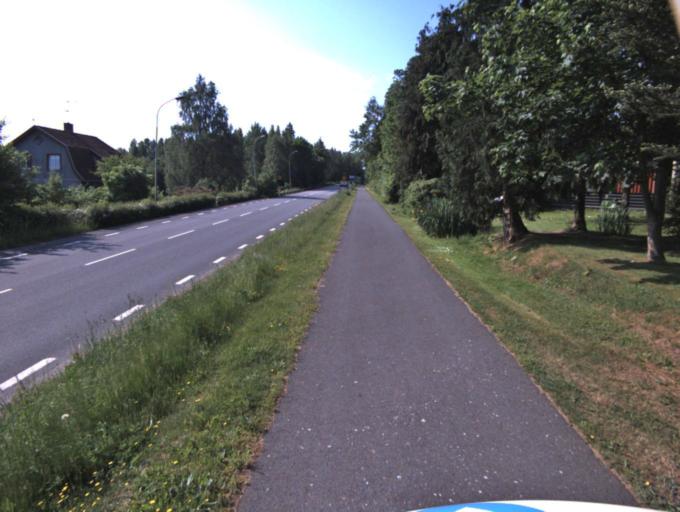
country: SE
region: Skane
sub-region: Kristianstads Kommun
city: Tollarp
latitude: 56.1705
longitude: 14.2821
